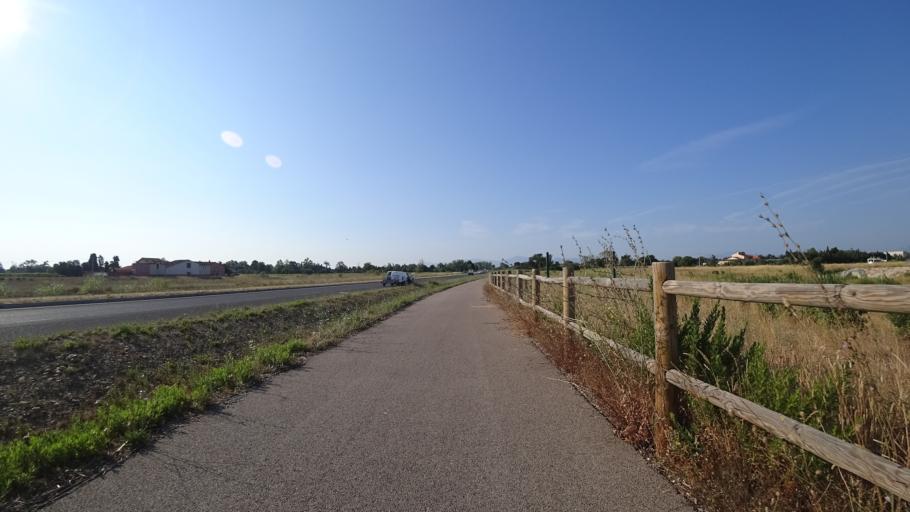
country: FR
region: Languedoc-Roussillon
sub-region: Departement des Pyrenees-Orientales
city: Pia
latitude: 42.7243
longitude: 2.9021
